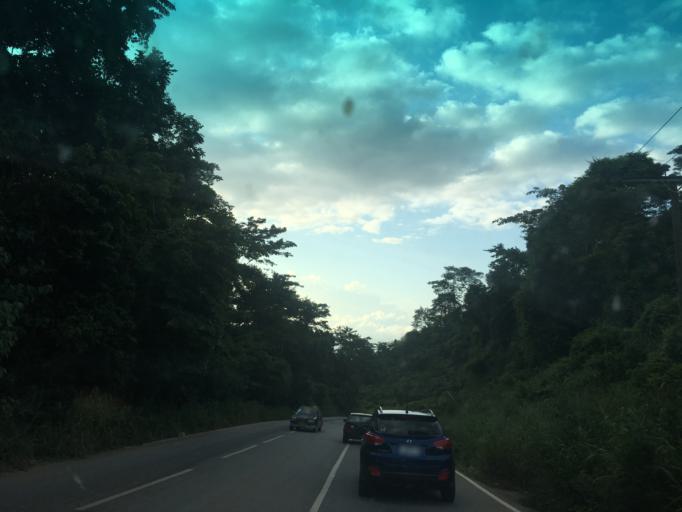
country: GH
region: Western
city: Bibiani
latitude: 6.4803
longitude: -2.3314
